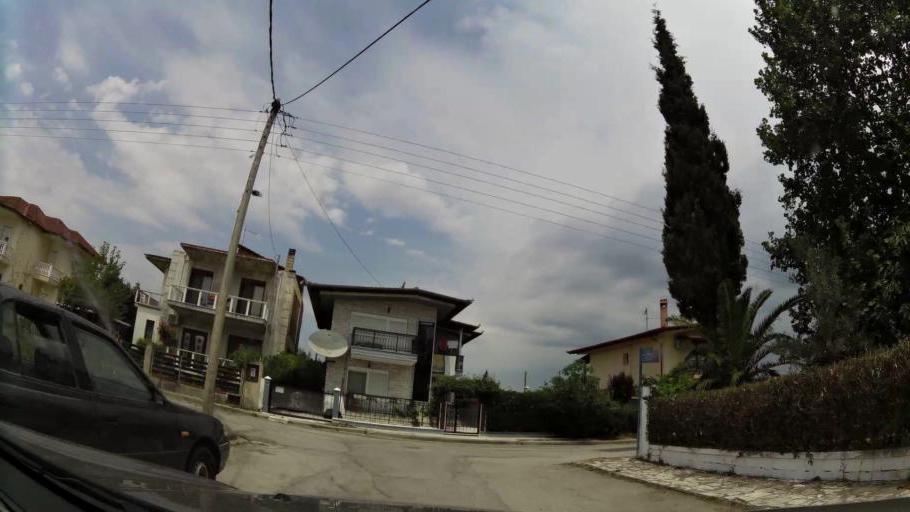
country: GR
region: Central Macedonia
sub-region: Nomos Pierias
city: Kallithea
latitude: 40.2676
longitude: 22.5810
